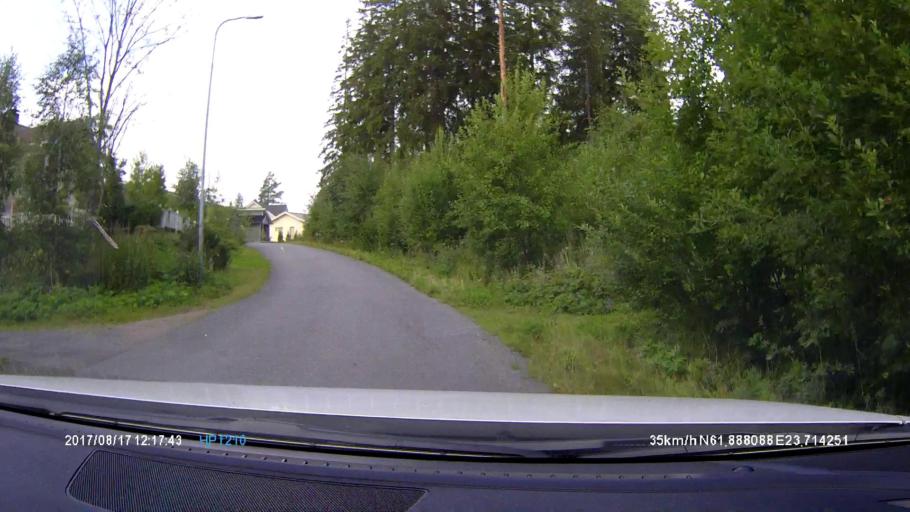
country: FI
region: Pirkanmaa
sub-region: Tampere
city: Kuru
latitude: 61.8883
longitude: 23.7138
